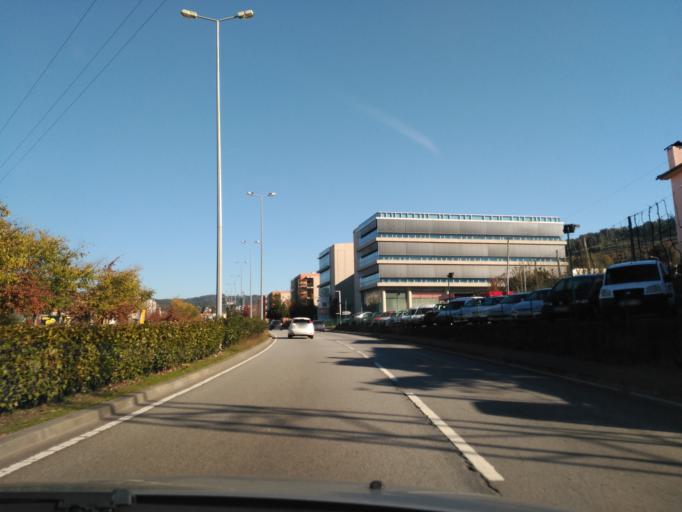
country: PT
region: Braga
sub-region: Braga
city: Adaufe
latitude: 41.5603
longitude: -8.3871
